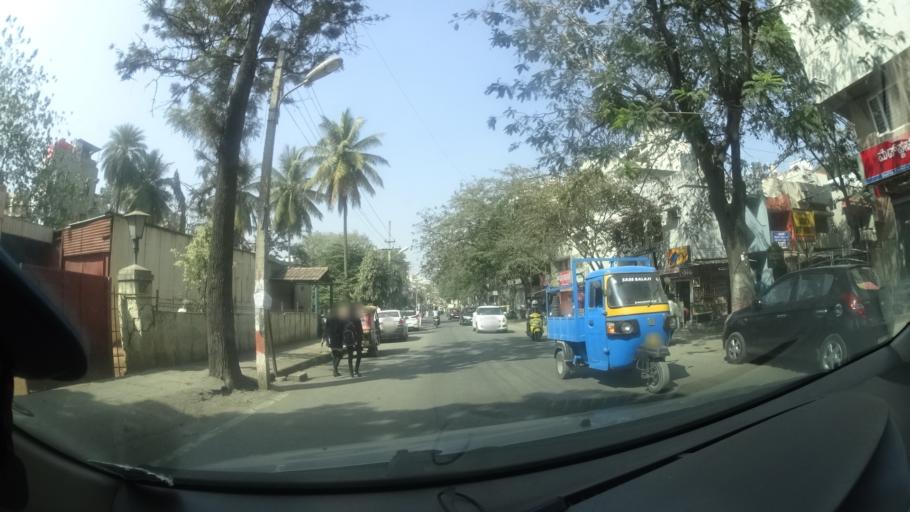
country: IN
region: Karnataka
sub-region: Bangalore Urban
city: Bangalore
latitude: 12.9990
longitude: 77.5762
